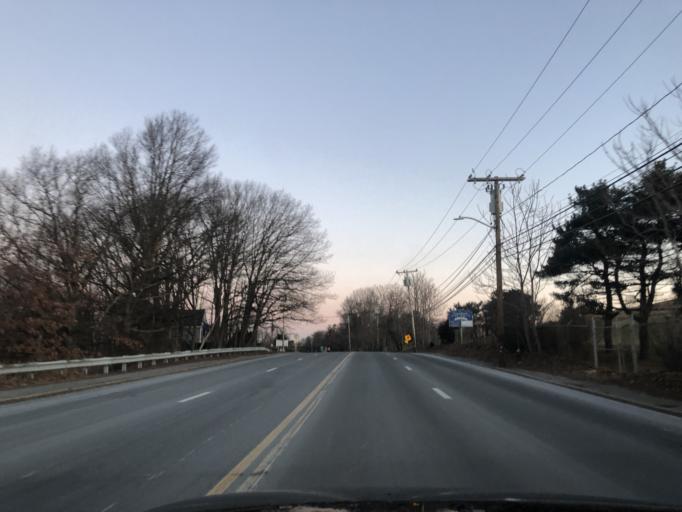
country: US
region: Massachusetts
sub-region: Norfolk County
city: Milton
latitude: 42.2691
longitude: -71.0464
